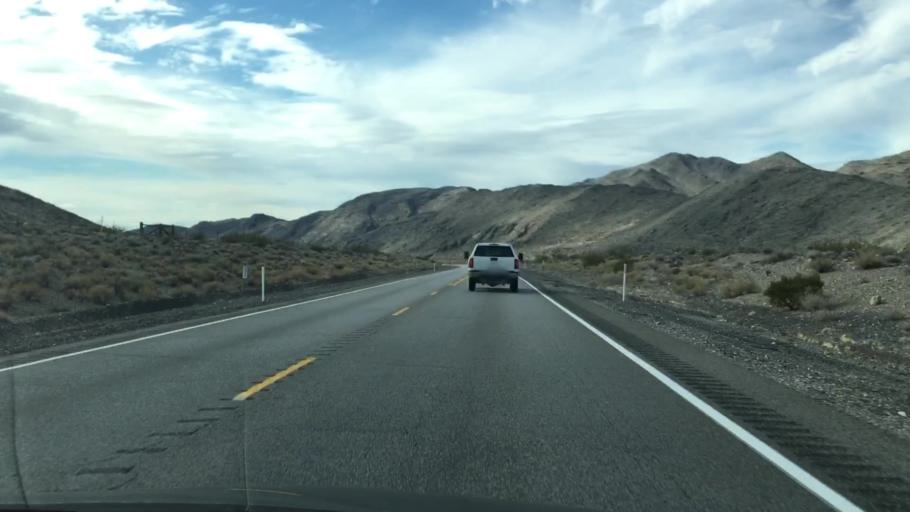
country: US
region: Nevada
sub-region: Nye County
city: Pahrump
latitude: 36.5885
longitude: -116.0500
